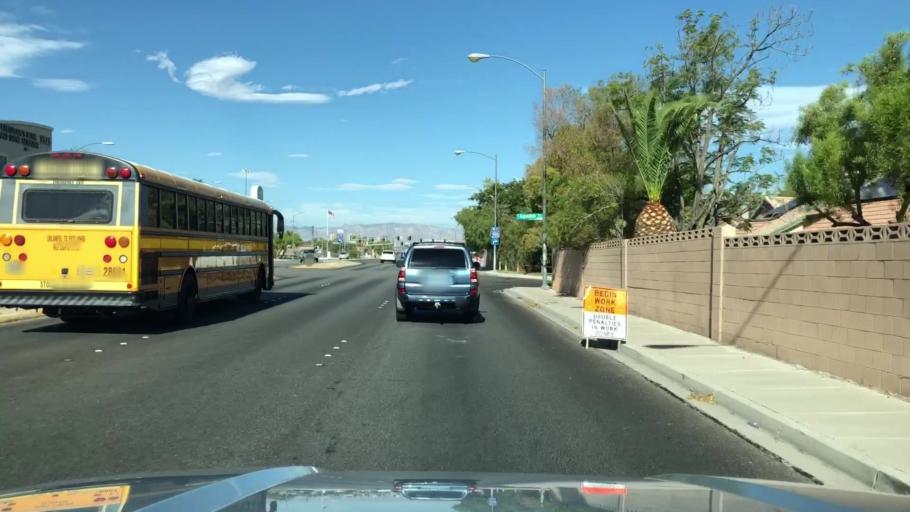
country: US
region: Nevada
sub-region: Clark County
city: Whitney
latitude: 36.0427
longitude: -115.1308
